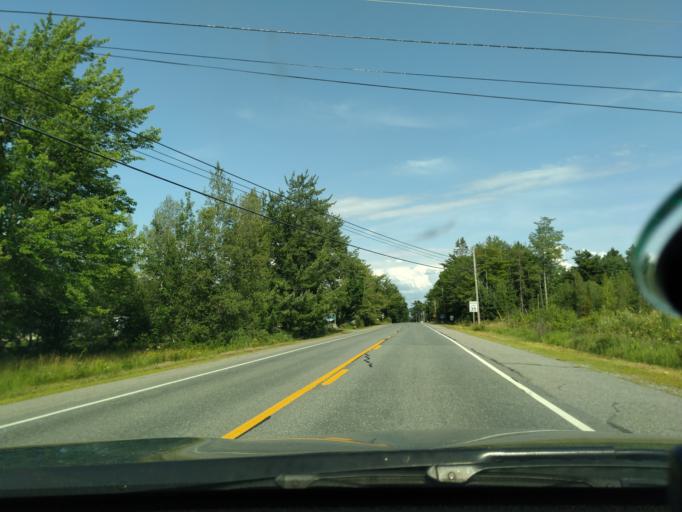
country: US
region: Maine
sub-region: Hancock County
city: Ellsworth
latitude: 44.5392
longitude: -68.4437
